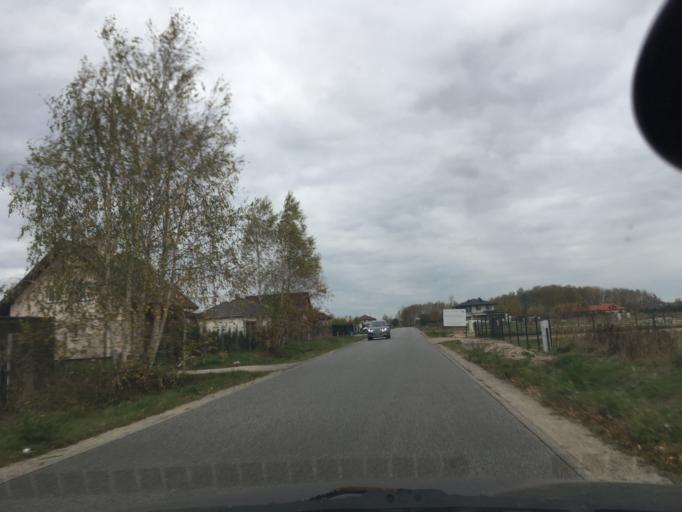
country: PL
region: Lodz Voivodeship
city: Zabia Wola
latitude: 52.0200
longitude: 20.7285
